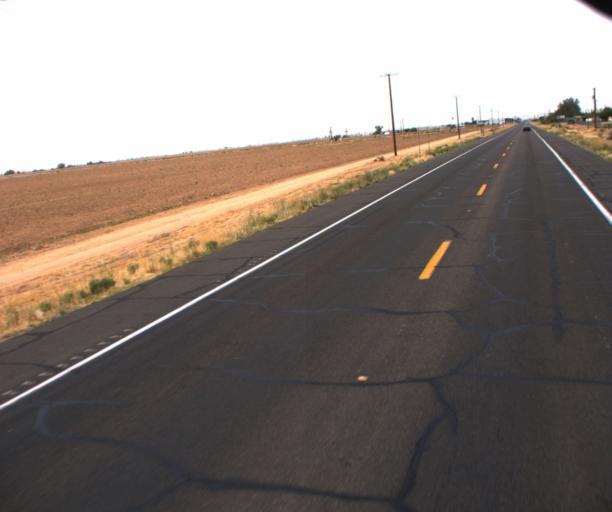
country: US
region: Arizona
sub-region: Pinal County
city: Coolidge
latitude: 32.9087
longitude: -111.5151
